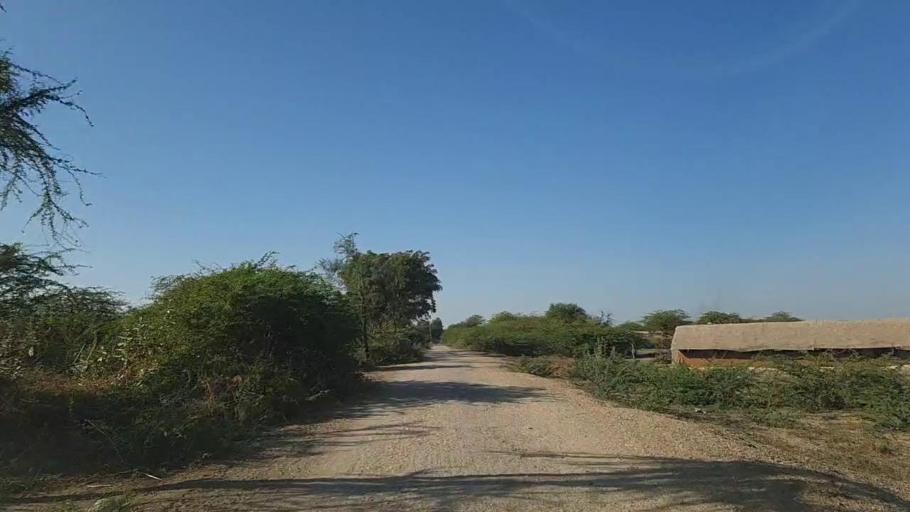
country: PK
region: Sindh
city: Samaro
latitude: 25.2637
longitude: 69.4861
